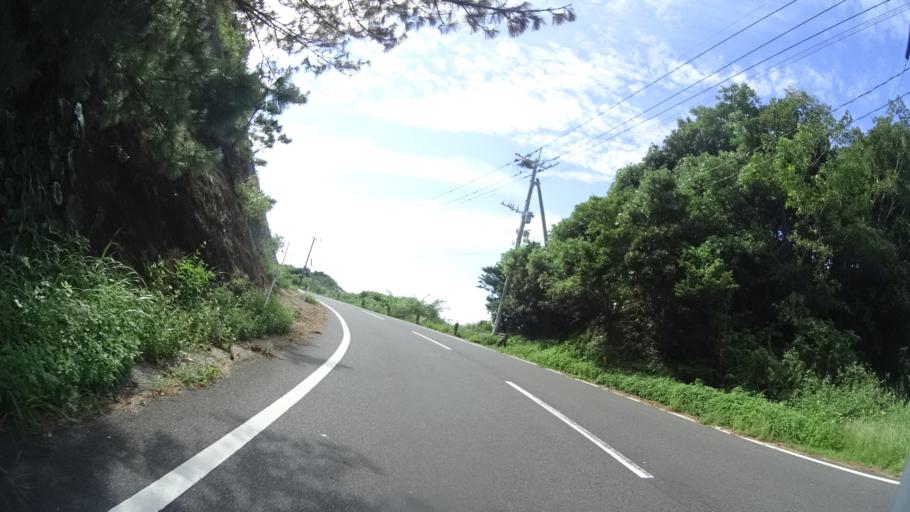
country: JP
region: Kagoshima
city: Nishinoomote
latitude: 30.4304
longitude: 130.4527
